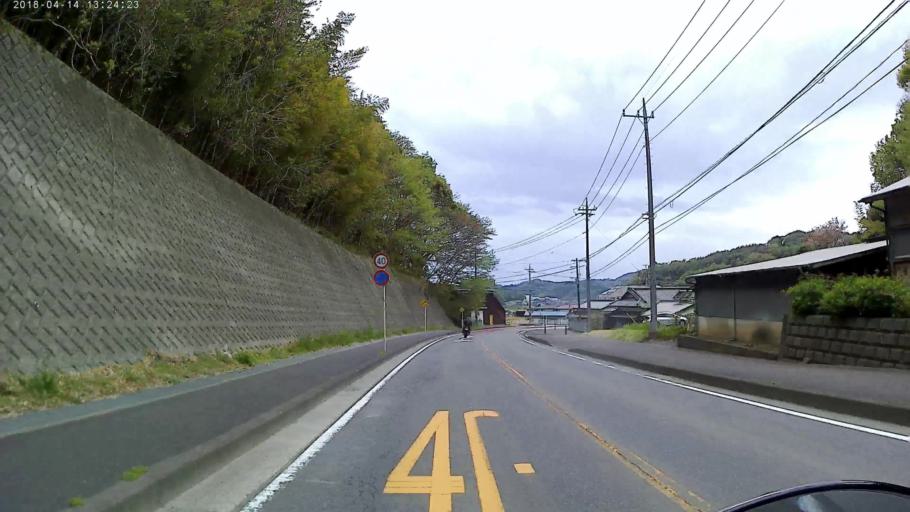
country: JP
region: Kanagawa
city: Hadano
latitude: 35.3332
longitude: 139.2200
